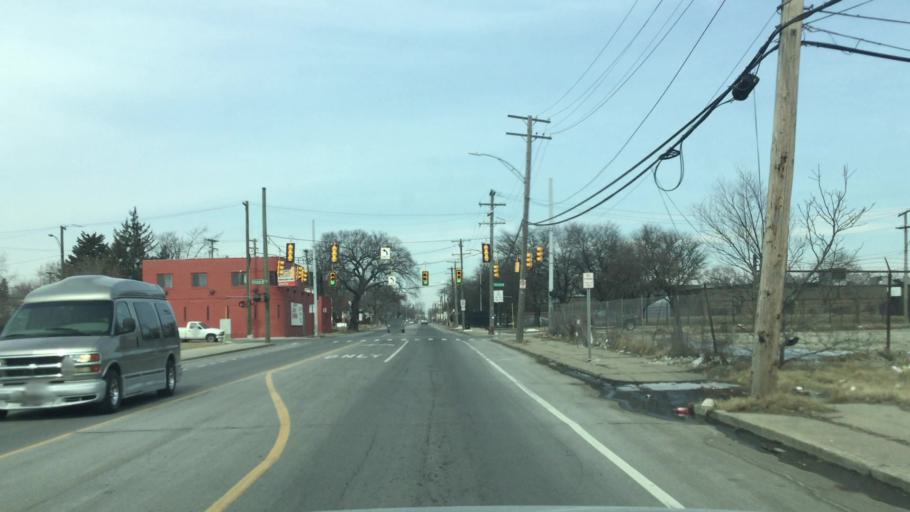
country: US
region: Michigan
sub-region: Wayne County
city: Dearborn
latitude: 42.3657
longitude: -83.1582
